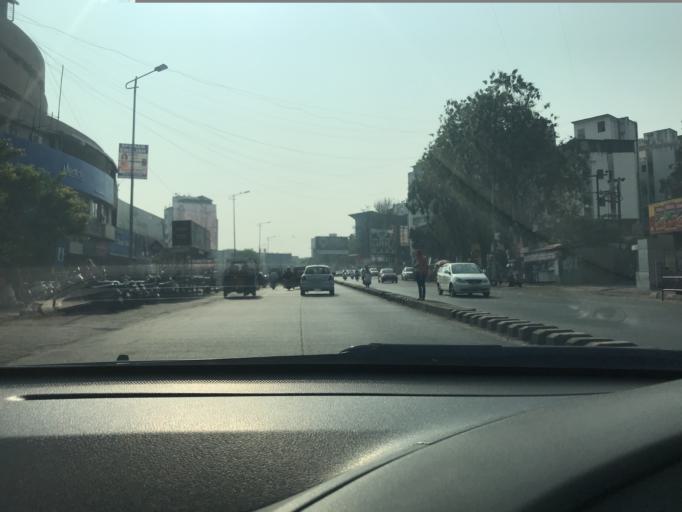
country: IN
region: Maharashtra
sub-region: Pune Division
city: Khadki
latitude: 18.5570
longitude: 73.7941
